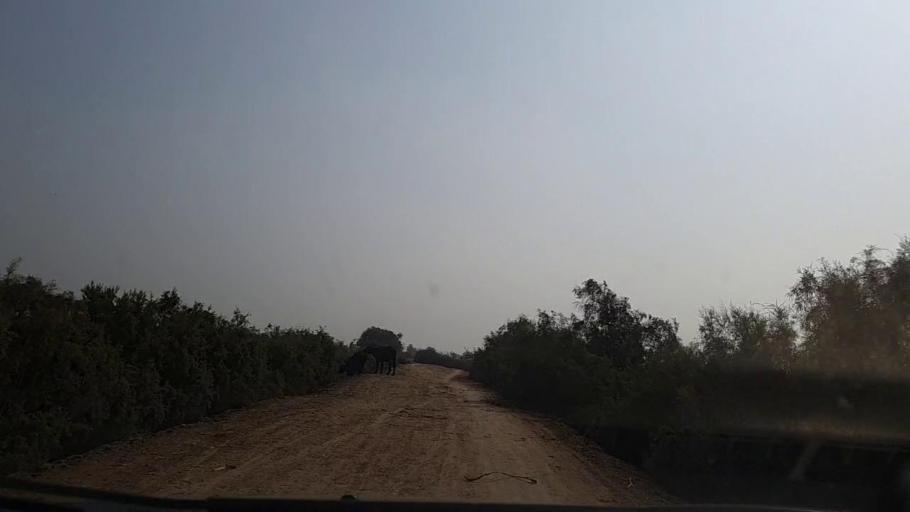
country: PK
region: Sindh
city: Sanghar
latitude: 26.0353
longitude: 68.9989
